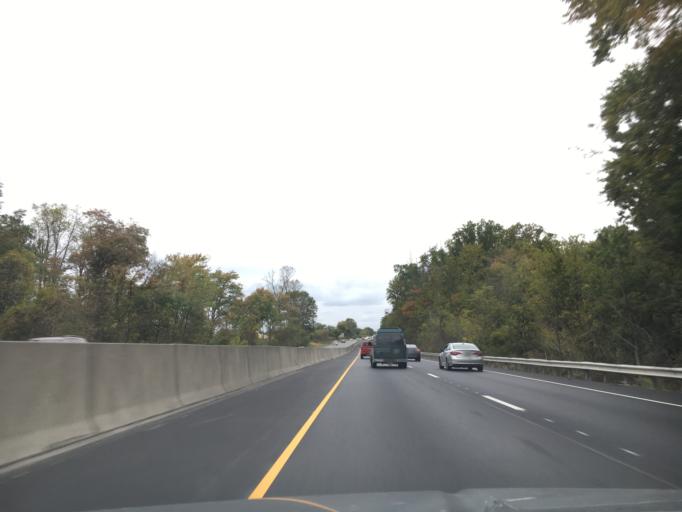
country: US
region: Pennsylvania
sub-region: Chester County
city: Downingtown
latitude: 40.0164
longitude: -75.7118
